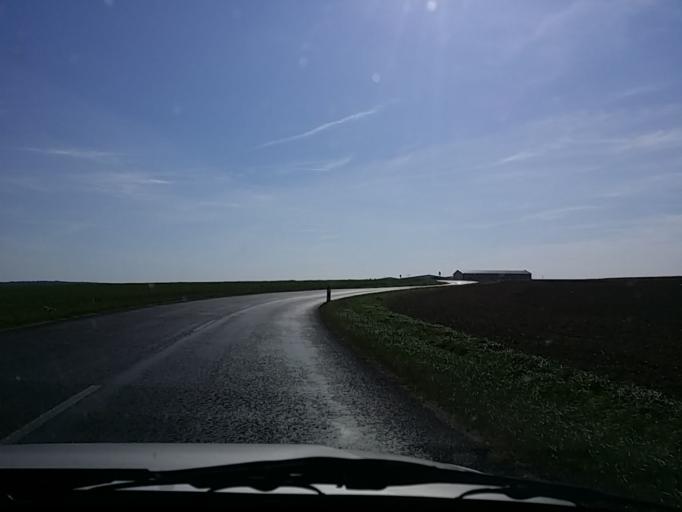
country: AT
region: Burgenland
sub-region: Politischer Bezirk Oberpullendorf
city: Lutzmannsburg
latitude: 47.4327
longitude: 16.6577
